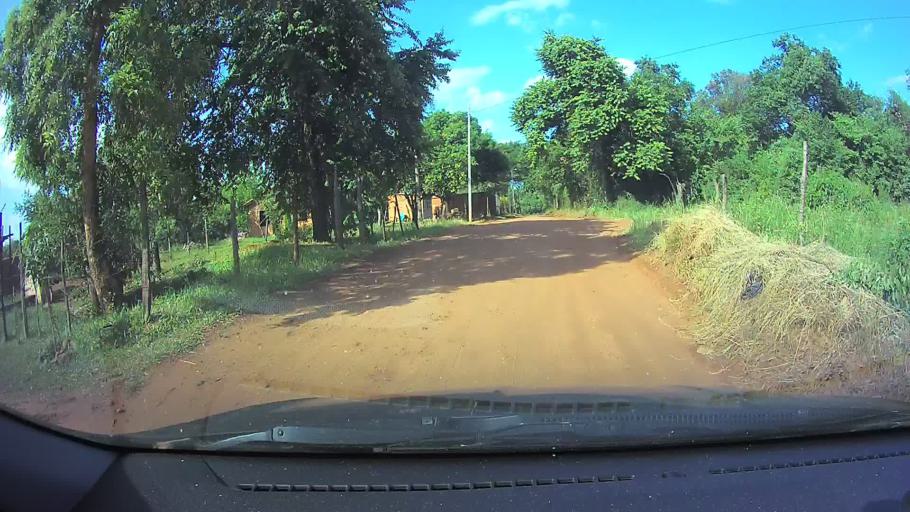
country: PY
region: Central
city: Limpio
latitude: -25.2406
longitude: -57.4651
